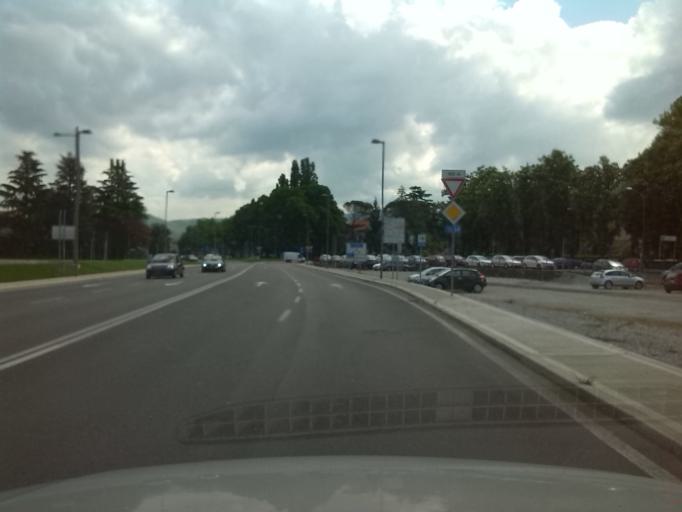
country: IT
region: Friuli Venezia Giulia
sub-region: Provincia di Udine
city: Cividale del Friuli
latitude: 46.0957
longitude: 13.4252
